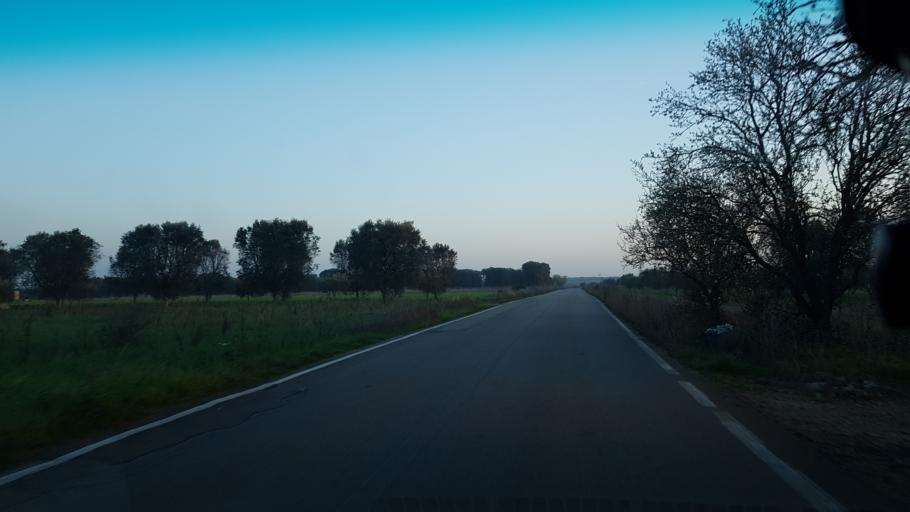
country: IT
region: Apulia
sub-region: Provincia di Brindisi
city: Mesagne
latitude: 40.6258
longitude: 17.7838
